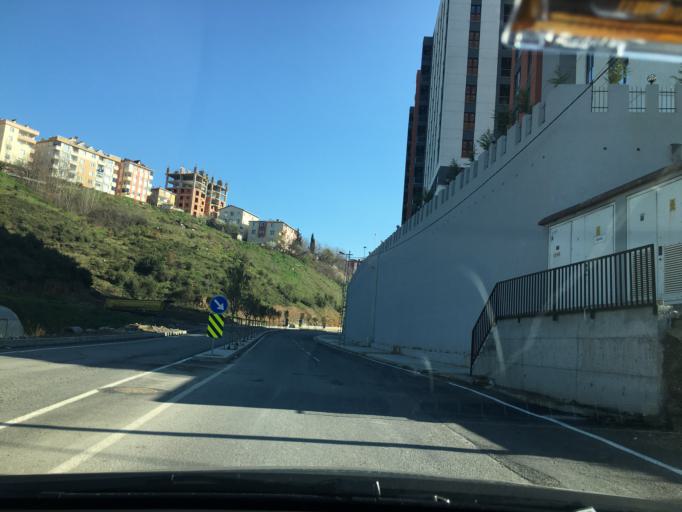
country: TR
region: Istanbul
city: Icmeler
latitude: 40.8719
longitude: 29.3013
